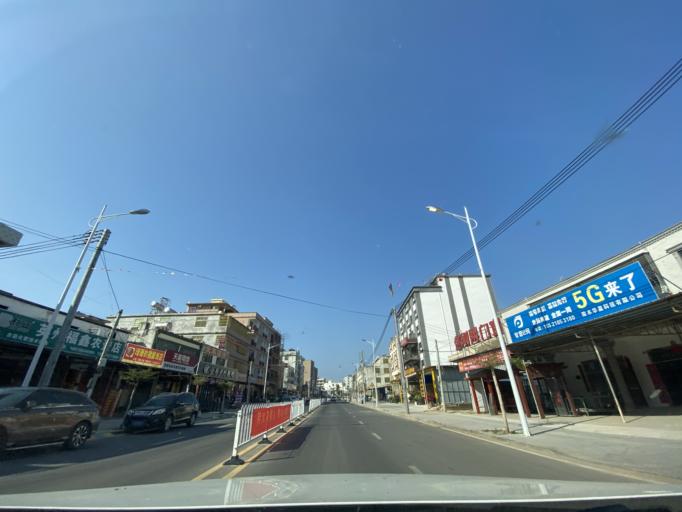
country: CN
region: Hainan
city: Yingzhou
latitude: 18.4178
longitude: 109.8539
